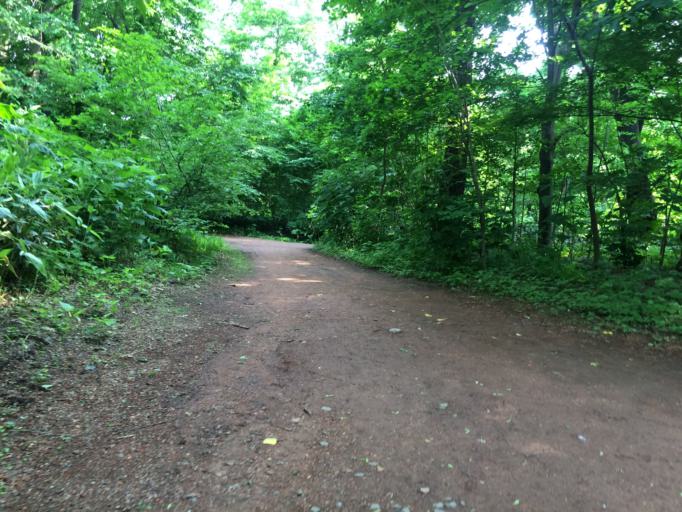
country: JP
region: Hokkaido
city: Sapporo
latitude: 43.0640
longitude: 141.3416
